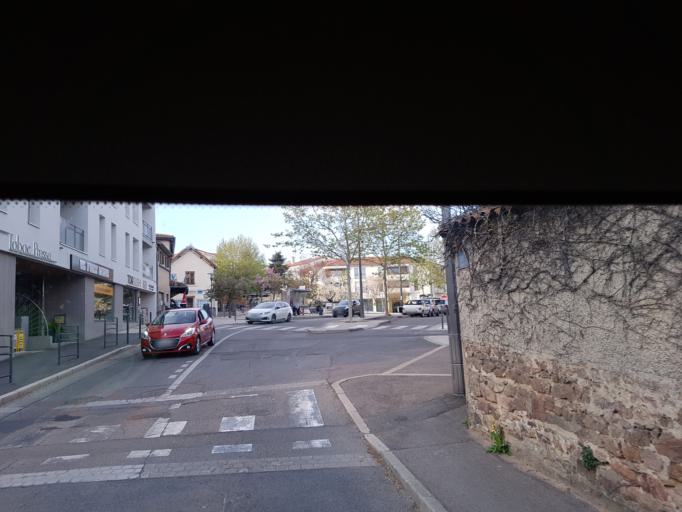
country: FR
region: Rhone-Alpes
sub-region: Departement du Rhone
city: Grezieu-la-Varenne
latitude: 45.7469
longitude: 4.6908
